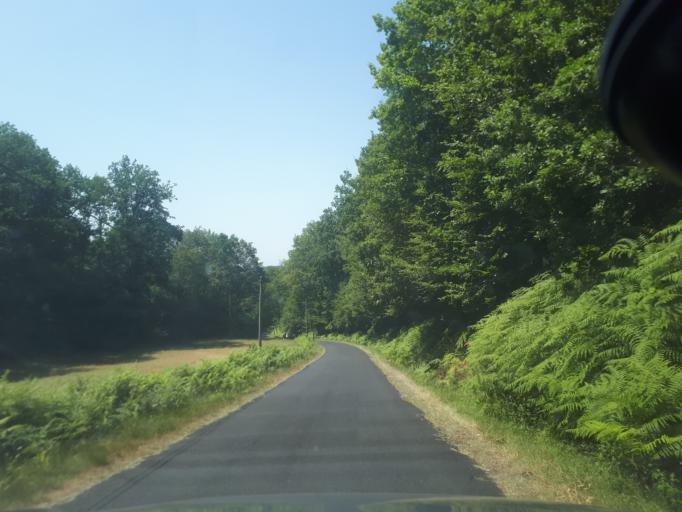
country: FR
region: Midi-Pyrenees
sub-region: Departement du Lot
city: Gourdon
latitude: 44.7356
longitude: 1.3193
